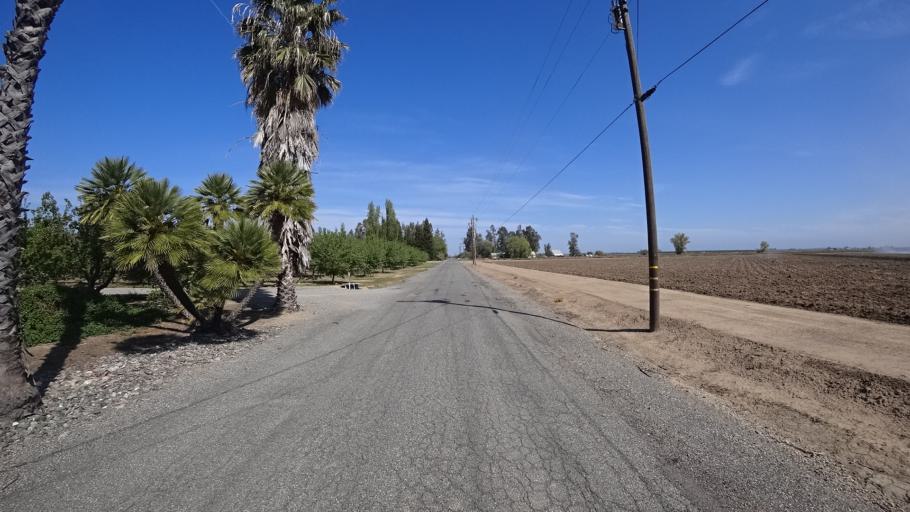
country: US
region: California
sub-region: Glenn County
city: Hamilton City
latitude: 39.5983
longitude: -122.0557
